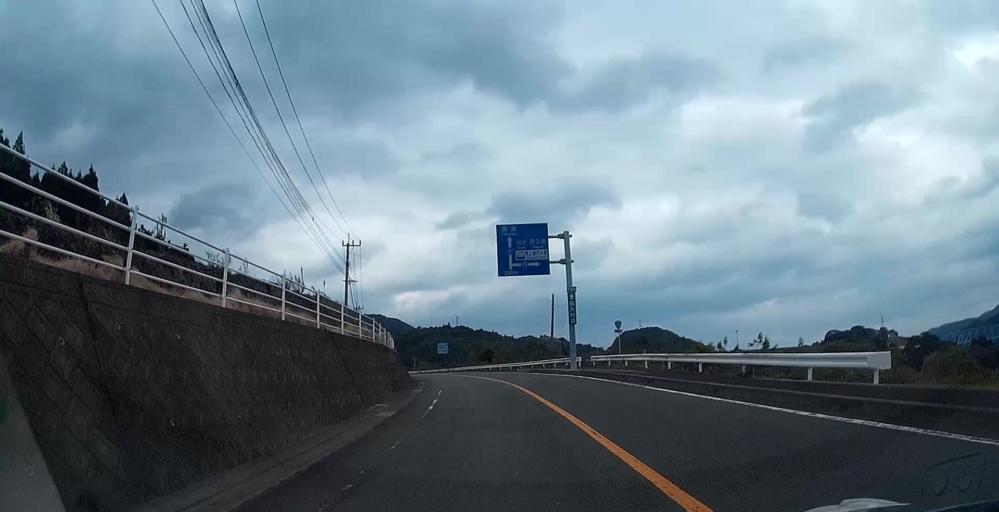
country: JP
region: Kagoshima
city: Akune
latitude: 32.1054
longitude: 130.1657
